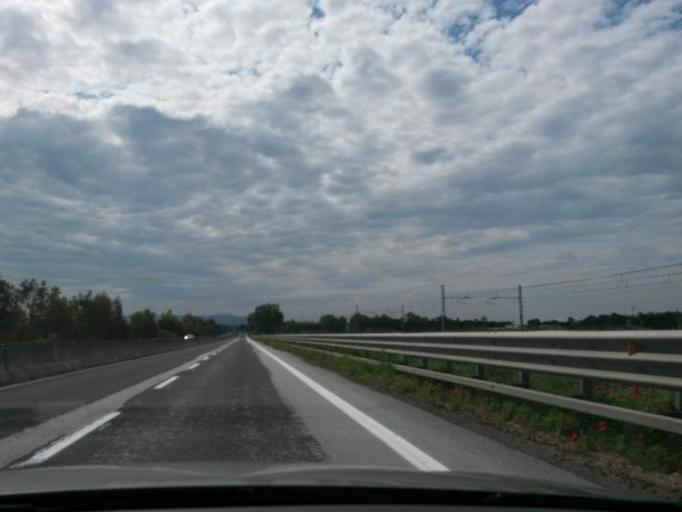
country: IT
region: Tuscany
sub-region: Provincia di Livorno
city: La California
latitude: 43.2555
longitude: 10.5462
